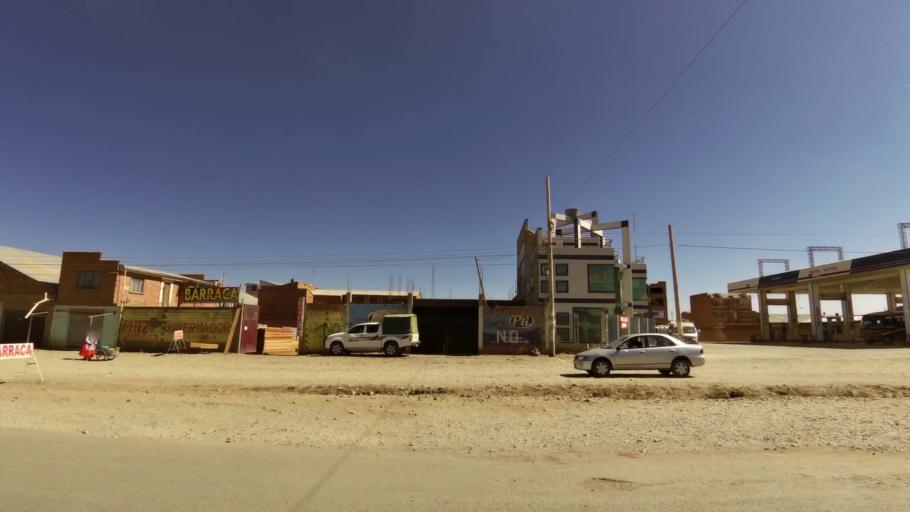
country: BO
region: La Paz
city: La Paz
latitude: -16.5498
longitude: -68.2048
